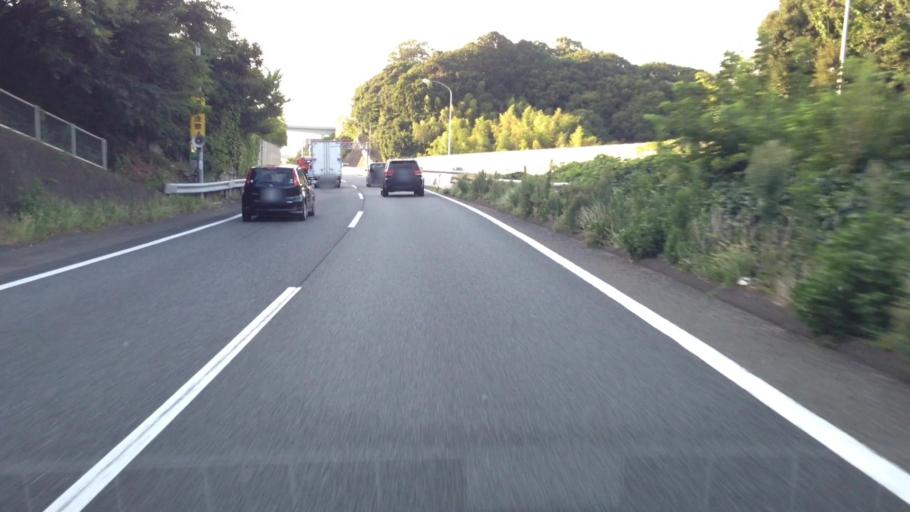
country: JP
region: Kanagawa
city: Kamakura
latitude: 35.3643
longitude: 139.5982
